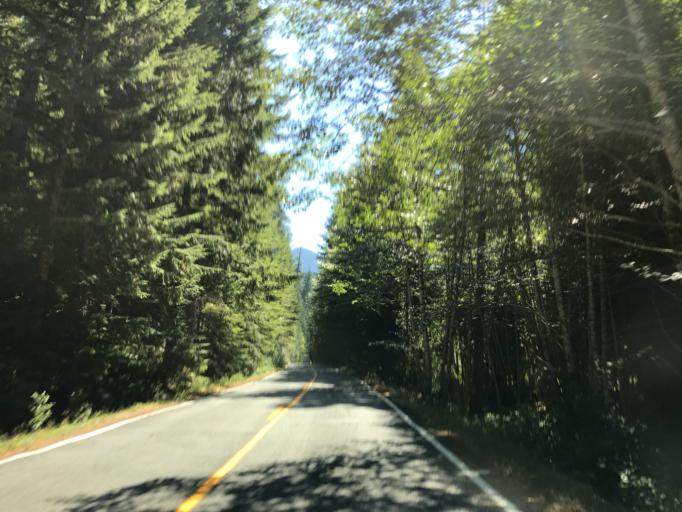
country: US
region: Washington
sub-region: Pierce County
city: Buckley
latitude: 46.7742
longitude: -121.5499
